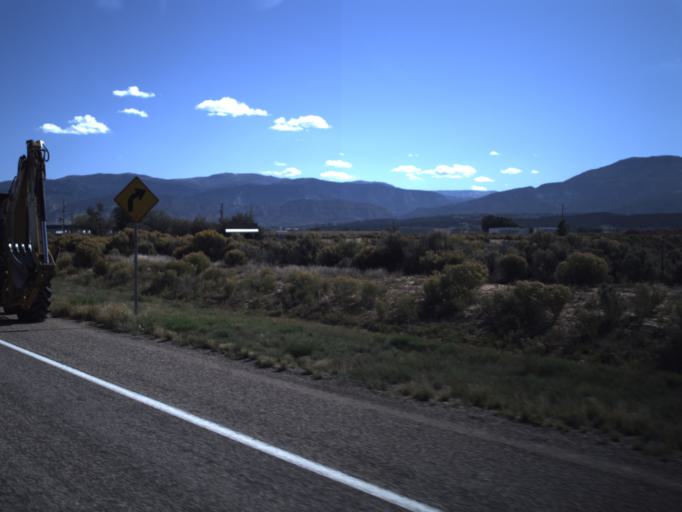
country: US
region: Utah
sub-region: Iron County
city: Cedar City
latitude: 37.6837
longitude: -113.1643
